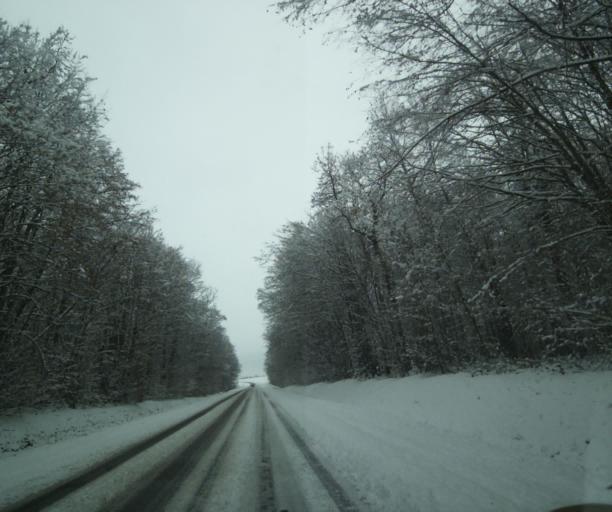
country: FR
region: Champagne-Ardenne
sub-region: Departement de la Haute-Marne
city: Montier-en-Der
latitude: 48.5257
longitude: 4.7985
